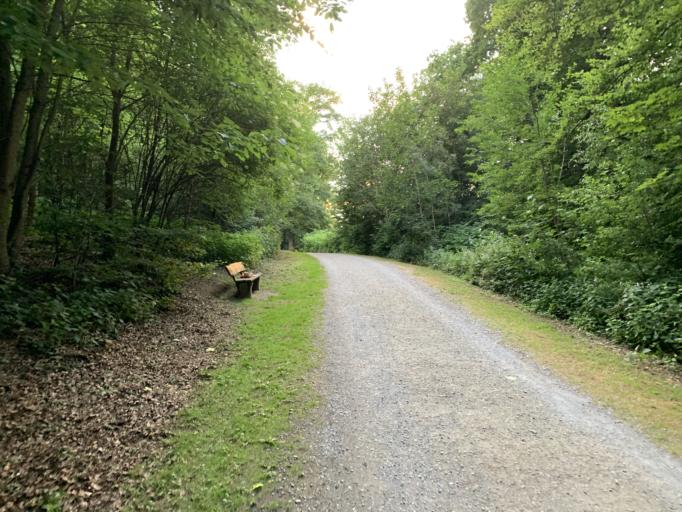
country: DE
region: North Rhine-Westphalia
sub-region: Regierungsbezirk Dusseldorf
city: Essen
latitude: 51.4207
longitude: 7.0092
